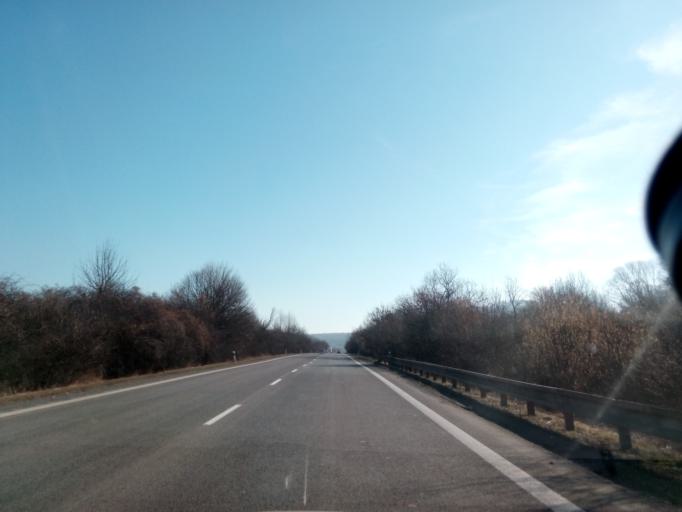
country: SK
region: Kosicky
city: Secovce
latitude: 48.7395
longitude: 21.4876
